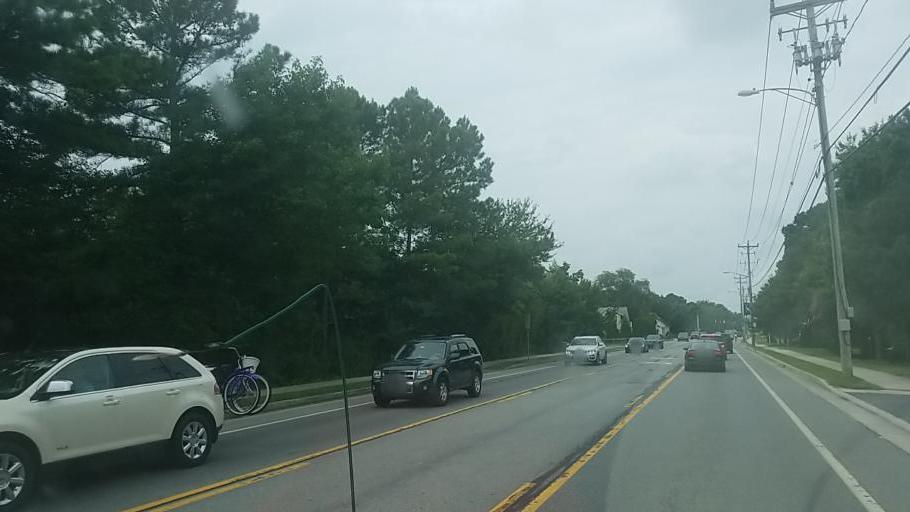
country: US
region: Delaware
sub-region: Sussex County
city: Bethany Beach
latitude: 38.5390
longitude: -75.0645
